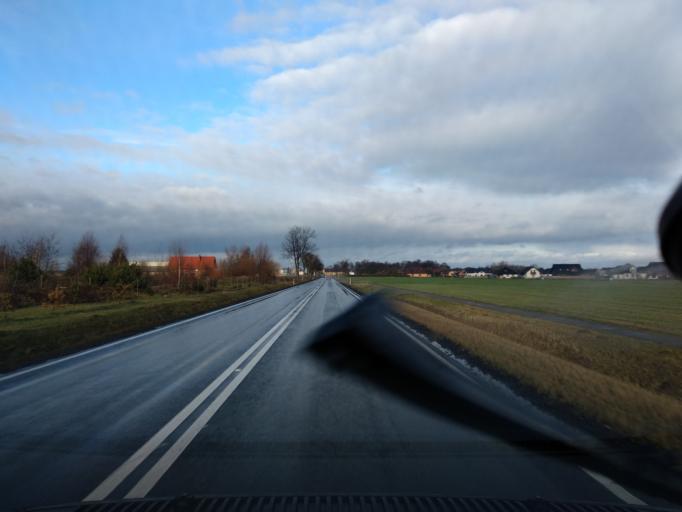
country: PL
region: Greater Poland Voivodeship
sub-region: Powiat koninski
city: Rychwal
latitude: 52.0600
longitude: 18.1636
